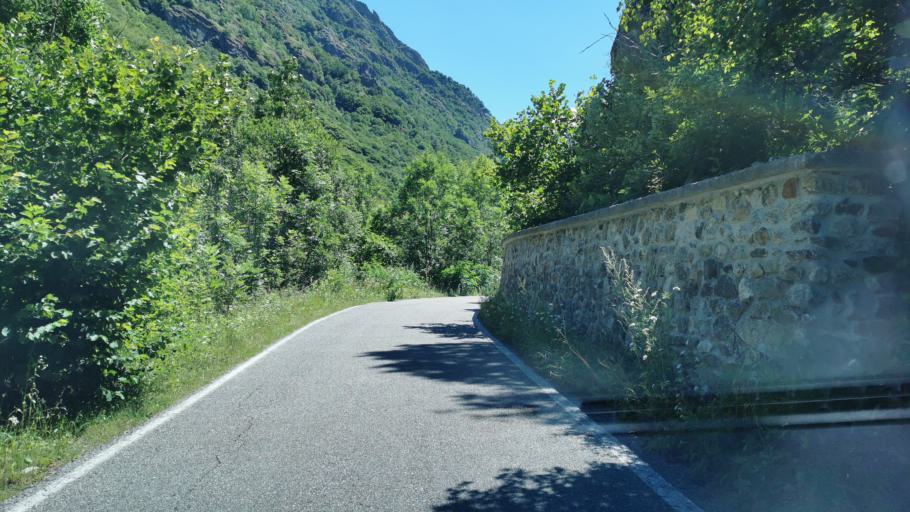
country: IT
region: Piedmont
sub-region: Provincia di Cuneo
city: Entracque
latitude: 44.1991
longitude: 7.3827
